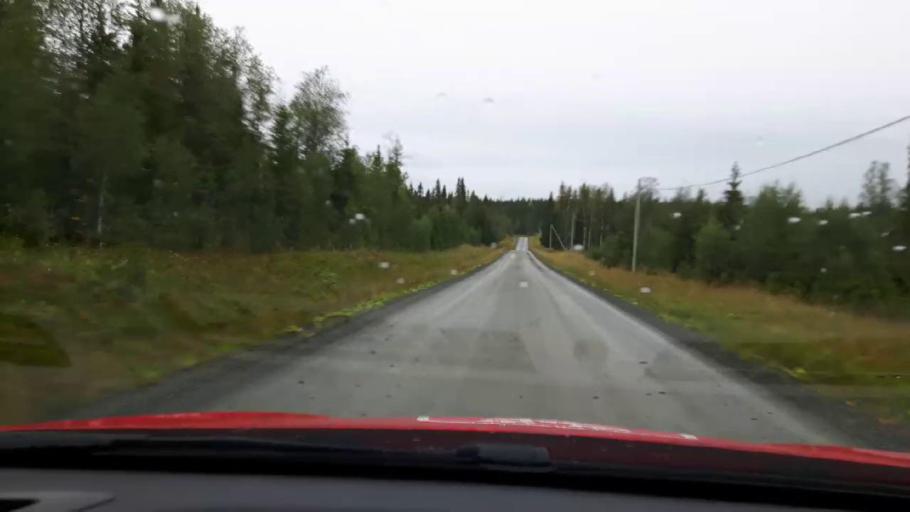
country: SE
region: Jaemtland
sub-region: Are Kommun
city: Are
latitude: 63.4387
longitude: 12.8074
